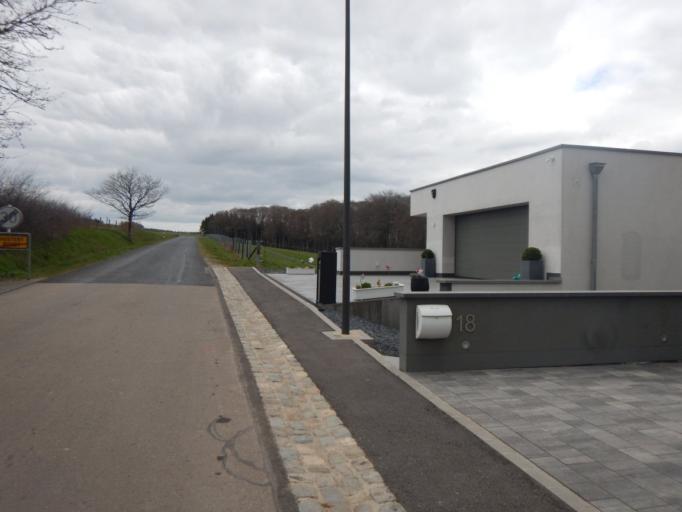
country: LU
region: Diekirch
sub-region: Canton de Redange
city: Rambrouch
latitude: 49.8000
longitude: 5.8226
